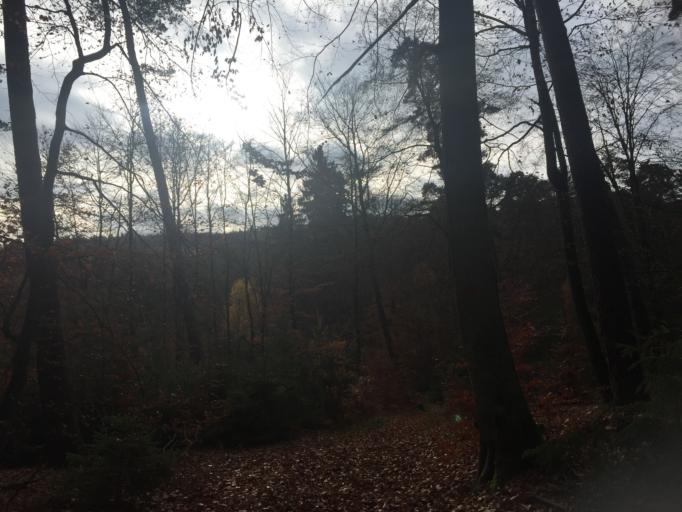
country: DE
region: Rheinland-Pfalz
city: Carlsberg
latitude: 49.4779
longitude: 8.0346
